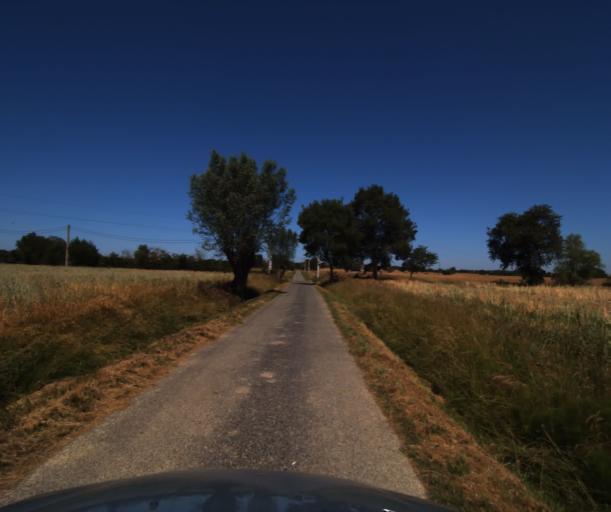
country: FR
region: Midi-Pyrenees
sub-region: Departement de la Haute-Garonne
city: Muret
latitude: 43.4527
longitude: 1.3673
